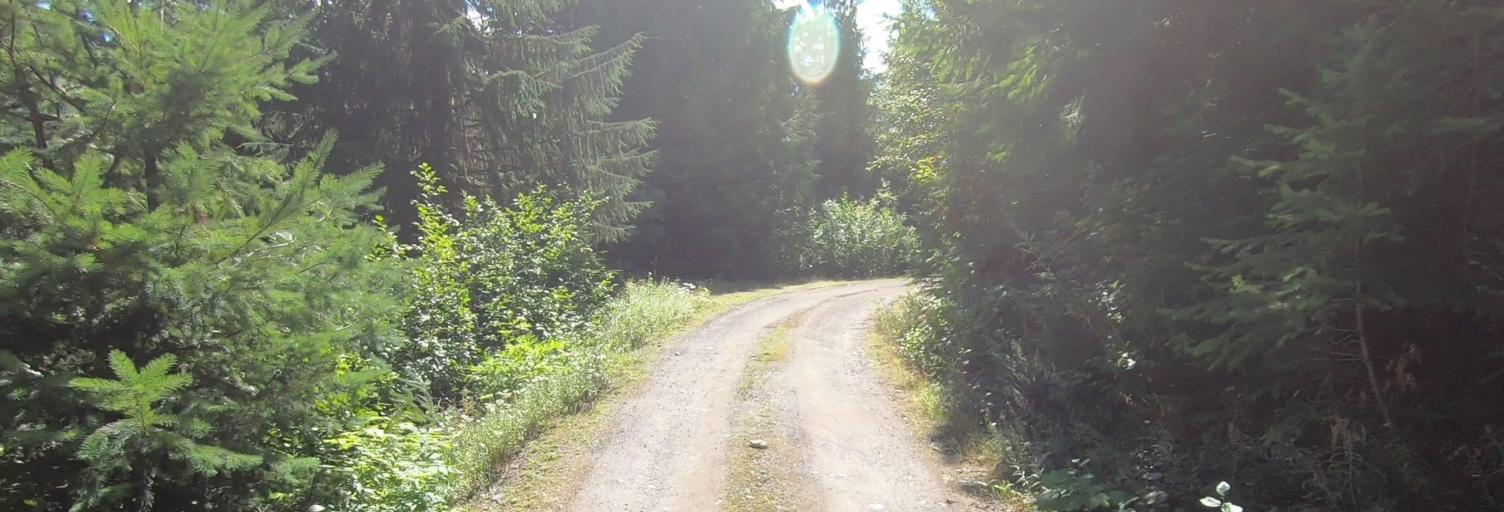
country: CA
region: British Columbia
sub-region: Fraser Valley Regional District
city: Chilliwack
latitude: 48.8549
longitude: -121.7811
